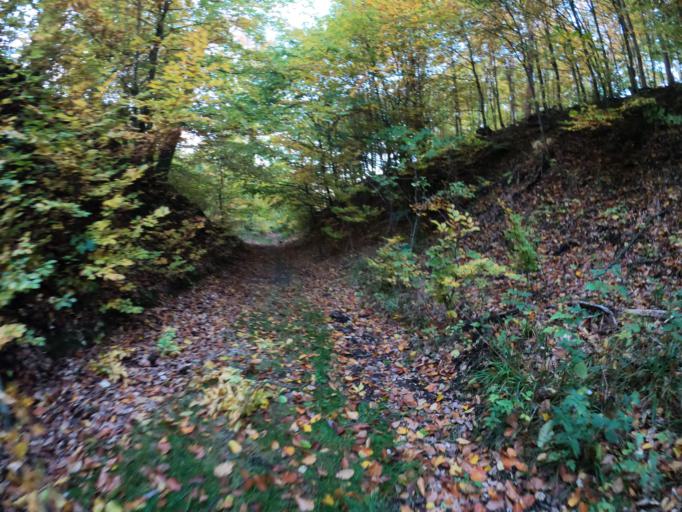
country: PL
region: West Pomeranian Voivodeship
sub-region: Powiat mysliborski
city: Barlinek
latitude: 52.9738
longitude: 15.2318
